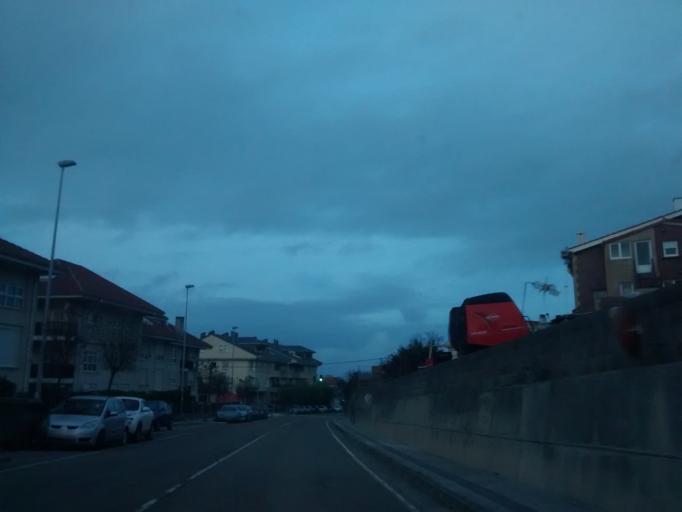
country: ES
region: Cantabria
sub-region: Provincia de Cantabria
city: Santa Cruz de Bezana
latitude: 43.4574
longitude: -3.9318
